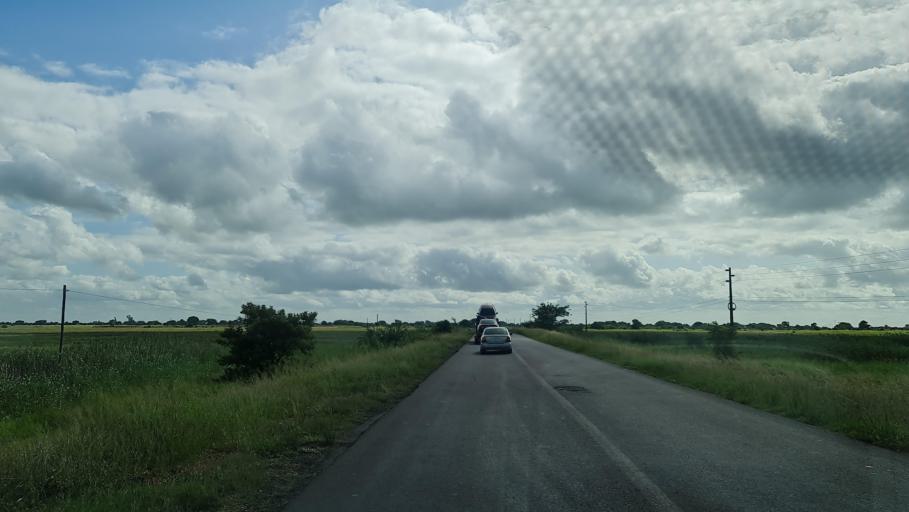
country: MZ
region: Gaza
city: Macia
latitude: -25.0951
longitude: 32.8324
